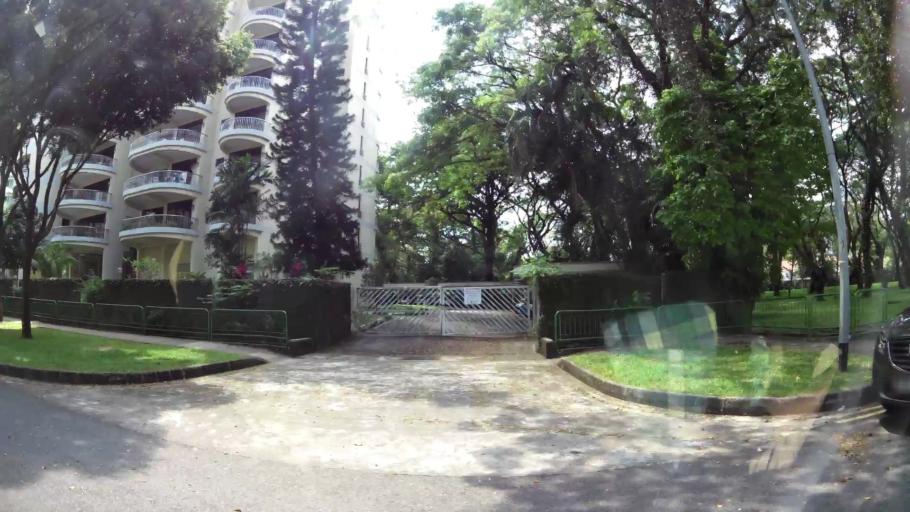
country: SG
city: Singapore
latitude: 1.3132
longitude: 103.8413
